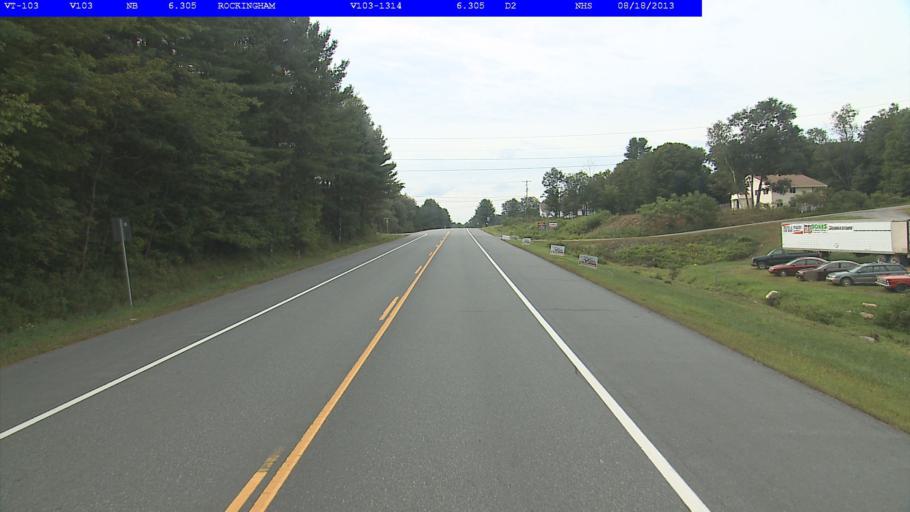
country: US
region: Vermont
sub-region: Windsor County
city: Chester
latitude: 43.2306
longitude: -72.5470
